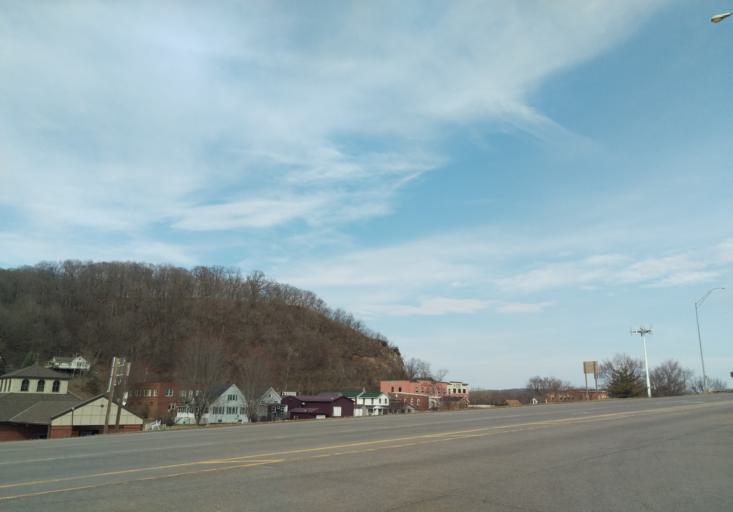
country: US
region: Wisconsin
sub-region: Crawford County
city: Prairie du Chien
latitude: 43.0436
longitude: -91.1810
